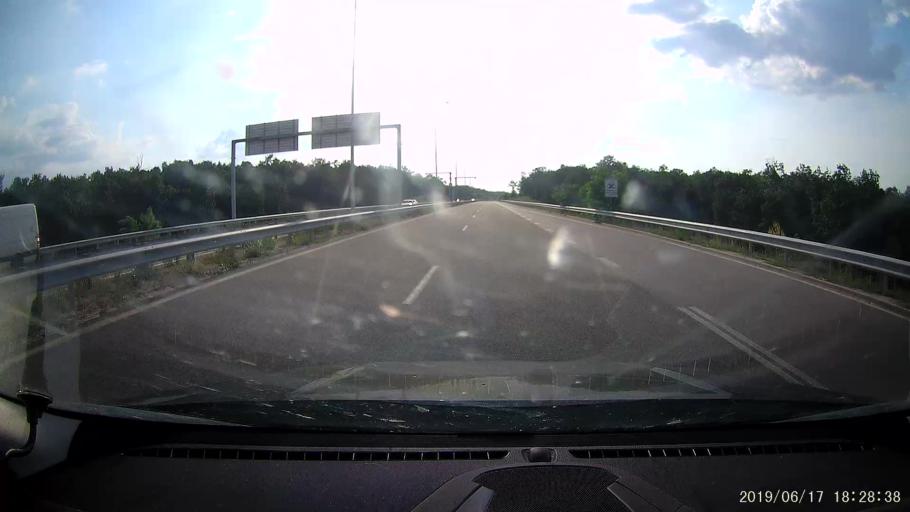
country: BG
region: Khaskovo
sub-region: Obshtina Dimitrovgrad
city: Dimitrovgrad
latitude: 42.0237
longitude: 25.5745
